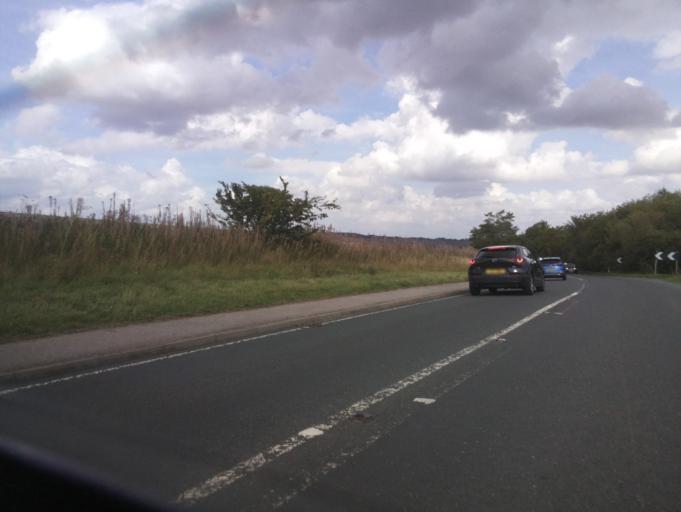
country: GB
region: England
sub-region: North Yorkshire
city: Catterick Garrison
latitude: 54.4127
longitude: -1.7036
